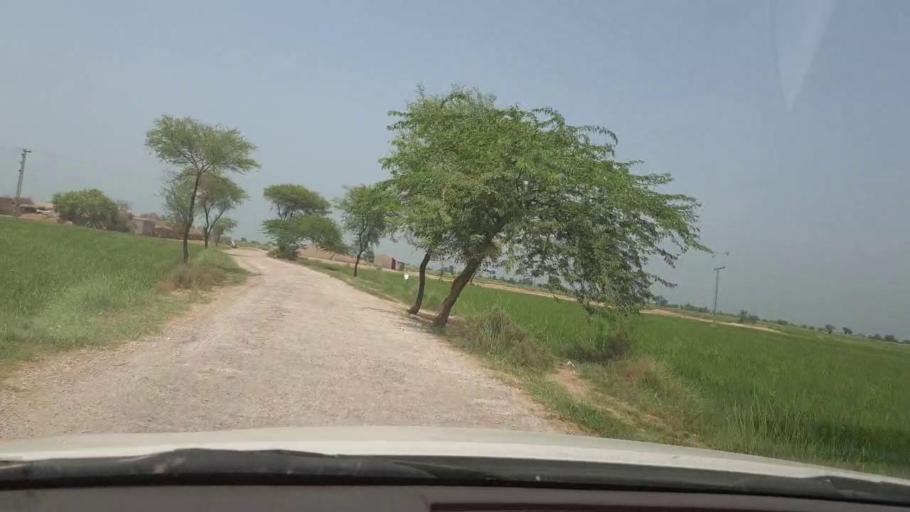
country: PK
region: Sindh
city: Shikarpur
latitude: 28.0713
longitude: 68.5754
